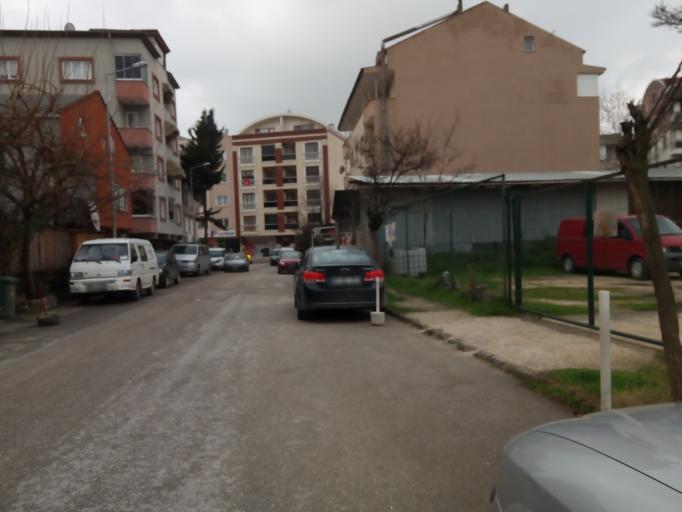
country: TR
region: Bursa
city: Niluefer
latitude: 40.2534
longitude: 28.9567
